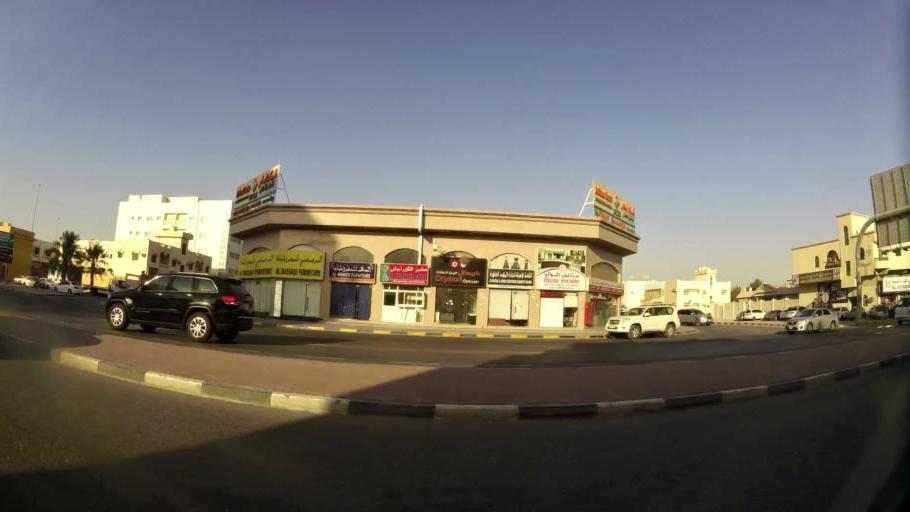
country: AE
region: Ajman
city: Ajman
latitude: 25.3971
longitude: 55.5047
